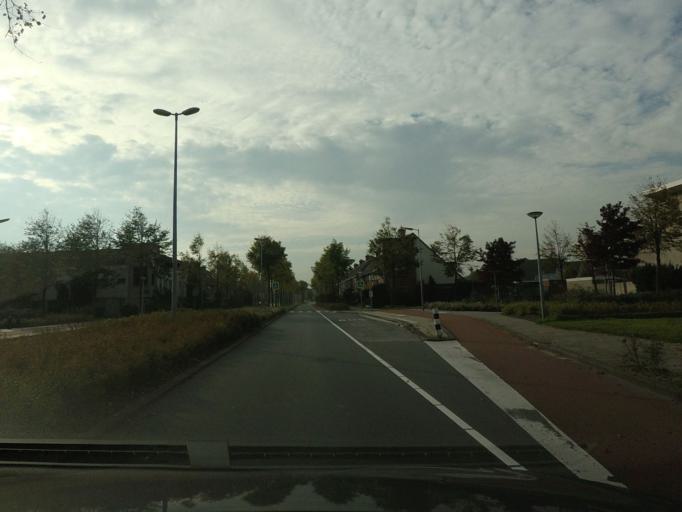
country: NL
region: North Holland
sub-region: Gemeente Langedijk
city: Broek op Langedijk
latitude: 52.6718
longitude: 4.7698
